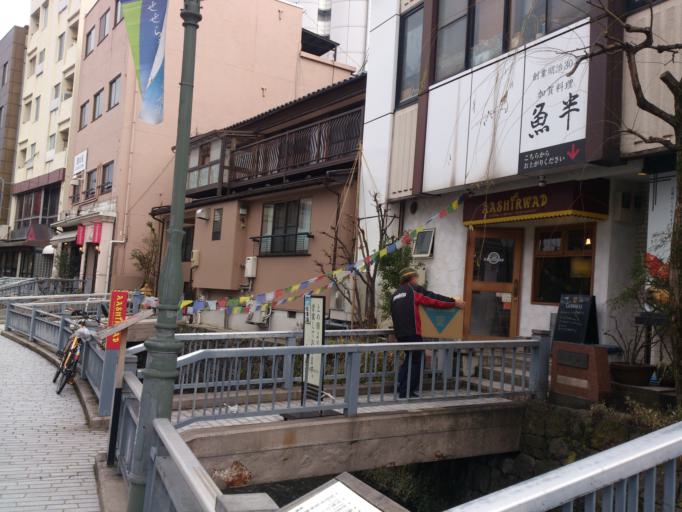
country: JP
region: Ishikawa
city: Kanazawa-shi
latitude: 36.5640
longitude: 136.6525
